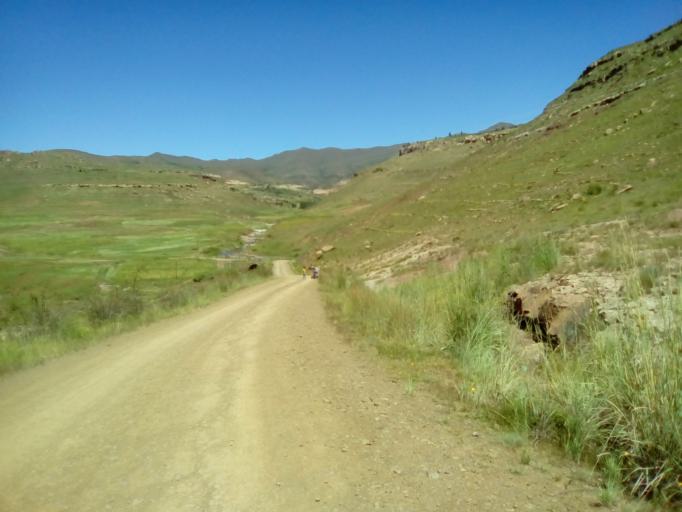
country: LS
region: Qacha's Nek
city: Qacha's Nek
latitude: -30.0366
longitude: 28.7281
